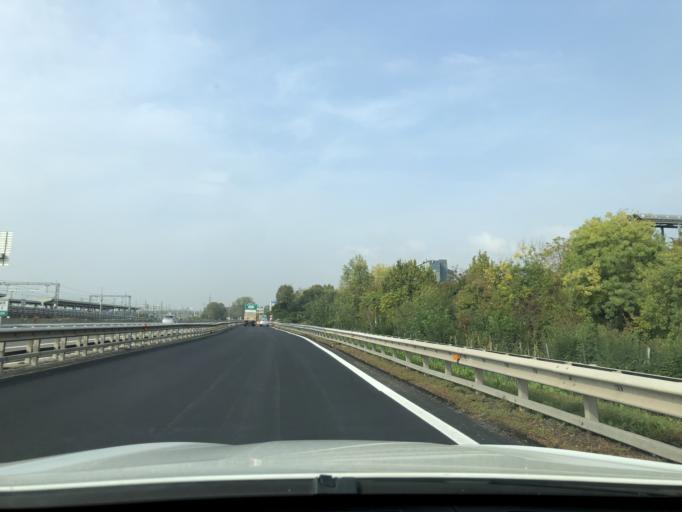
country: IT
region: Lombardy
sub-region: Citta metropolitana di Milano
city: San Donato Milanese
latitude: 45.4175
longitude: 9.2540
